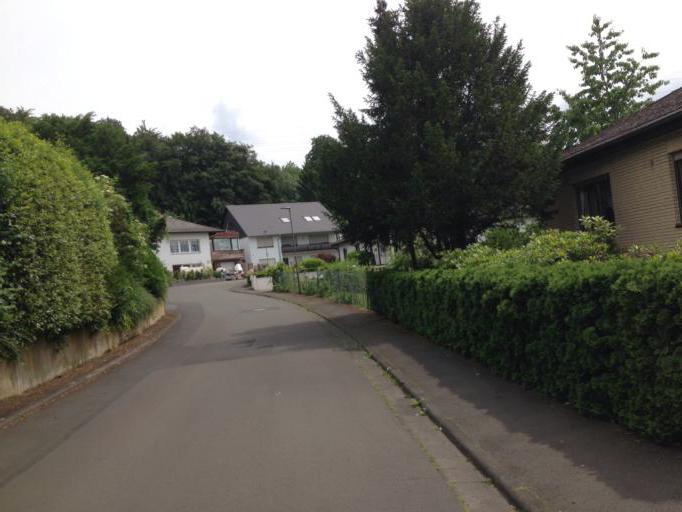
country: DE
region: Hesse
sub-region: Regierungsbezirk Giessen
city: Alten Buseck
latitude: 50.5934
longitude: 8.7485
